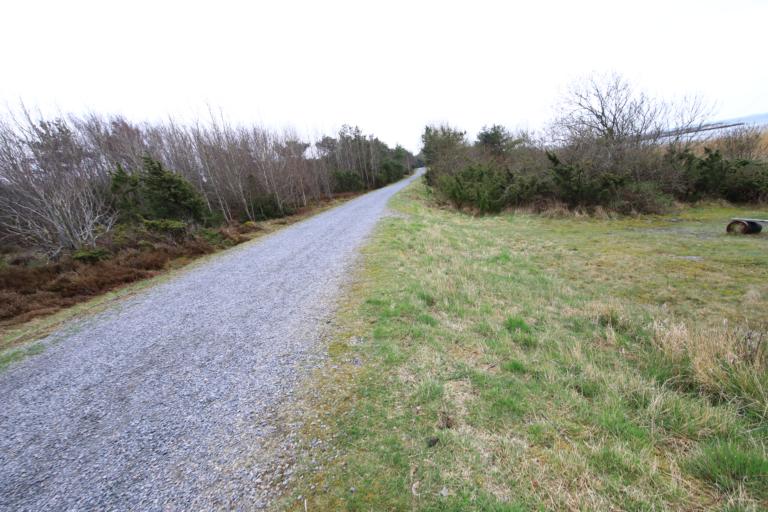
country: SE
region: Halland
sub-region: Kungsbacka Kommun
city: Frillesas
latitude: 57.3012
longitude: 12.1672
